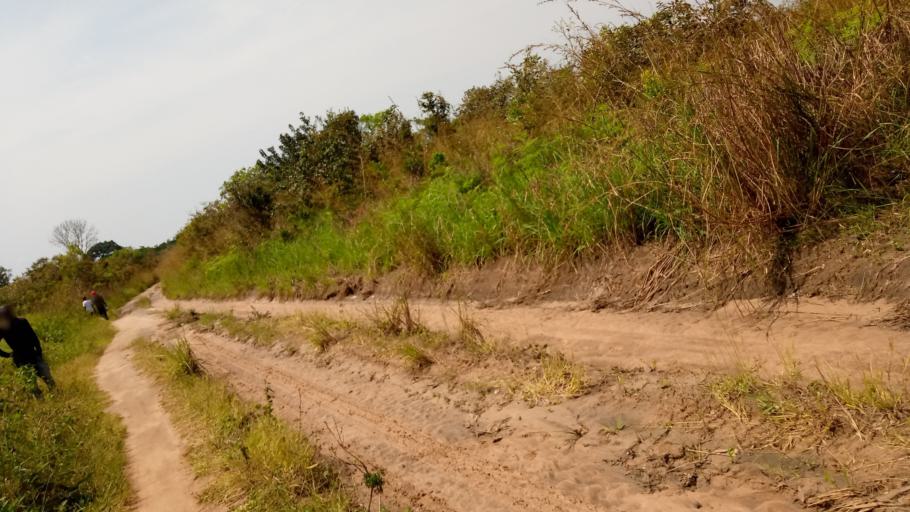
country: CD
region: Bandundu
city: Bandundu
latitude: -4.1701
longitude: 17.3969
